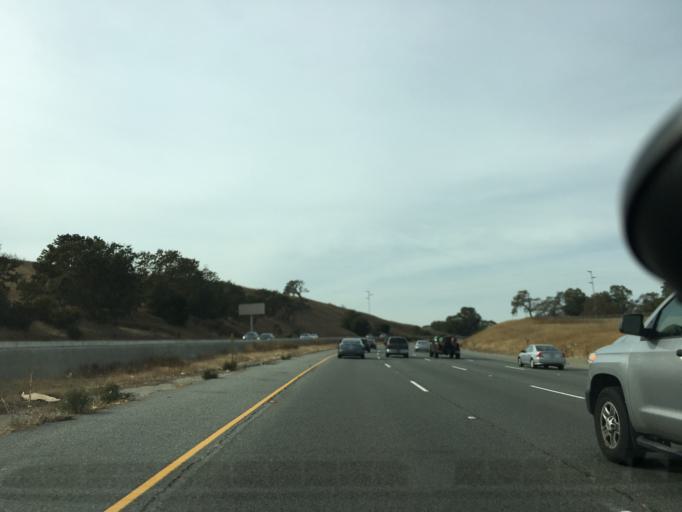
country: US
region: California
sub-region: San Mateo County
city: Ladera
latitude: 37.4128
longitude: -122.2061
